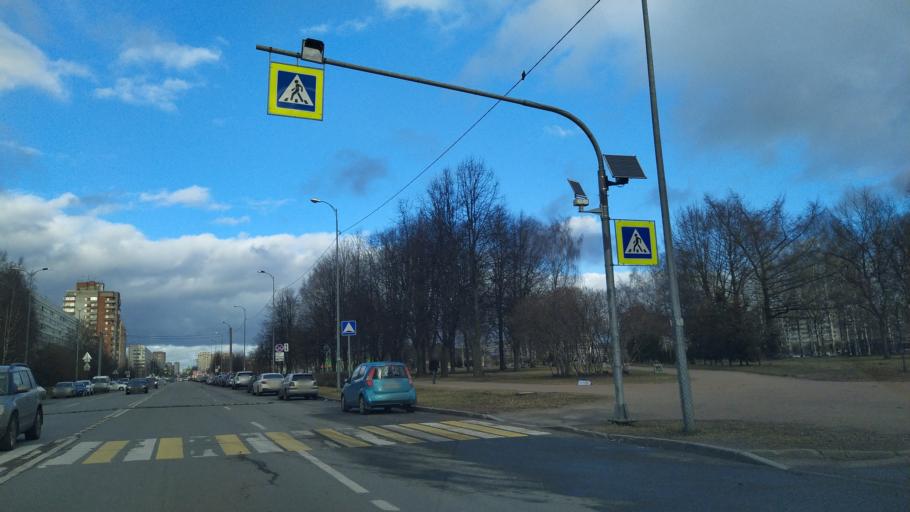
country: RU
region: St.-Petersburg
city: Grazhdanka
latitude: 60.0382
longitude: 30.3831
